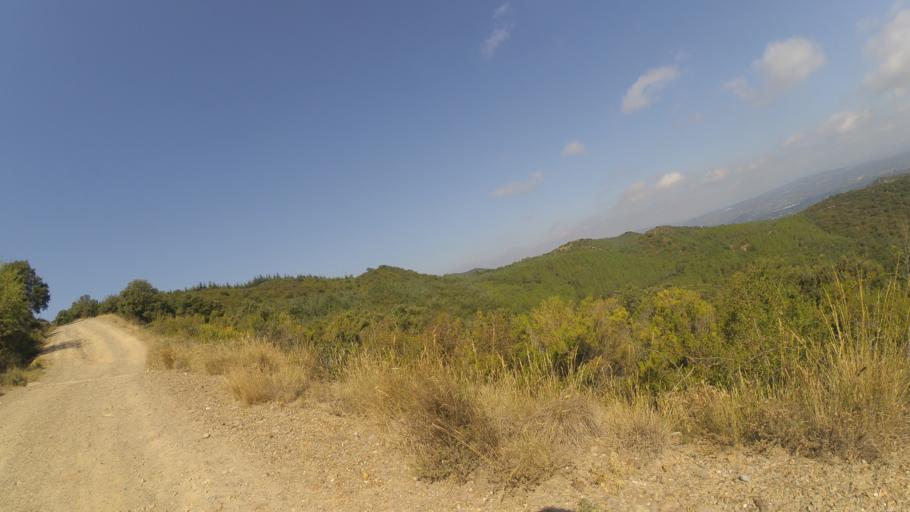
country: FR
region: Languedoc-Roussillon
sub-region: Departement des Pyrenees-Orientales
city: Millas
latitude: 42.6276
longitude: 2.6772
